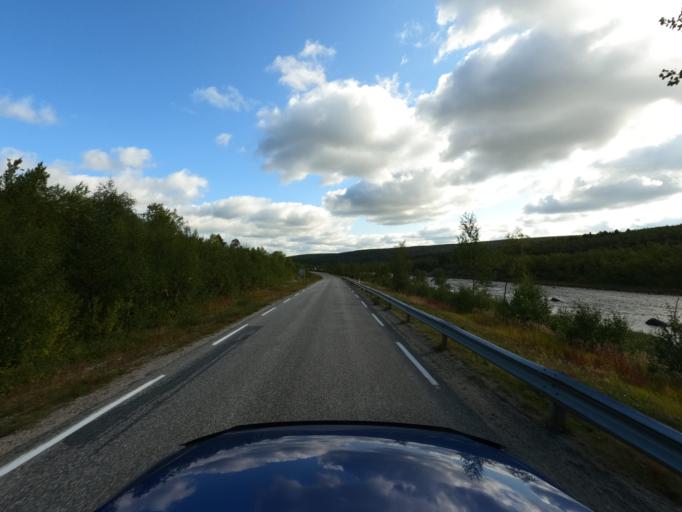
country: NO
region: Finnmark Fylke
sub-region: Porsanger
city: Lakselv
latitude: 69.4222
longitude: 24.8173
